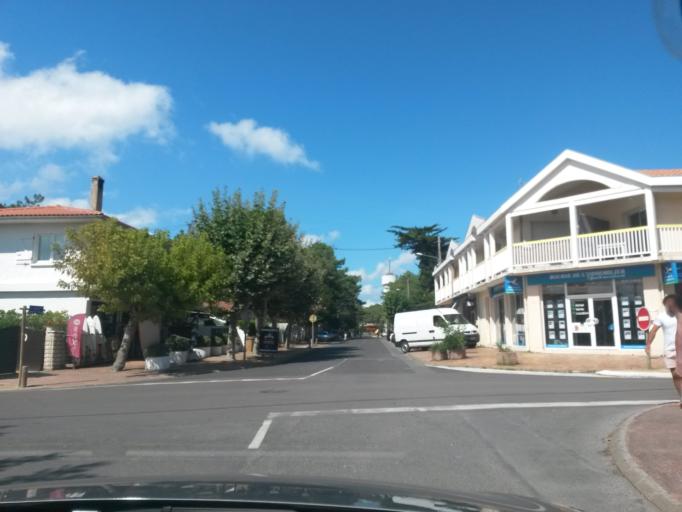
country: FR
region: Aquitaine
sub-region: Departement de la Gironde
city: Arcachon
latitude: 44.6481
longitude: -1.2488
